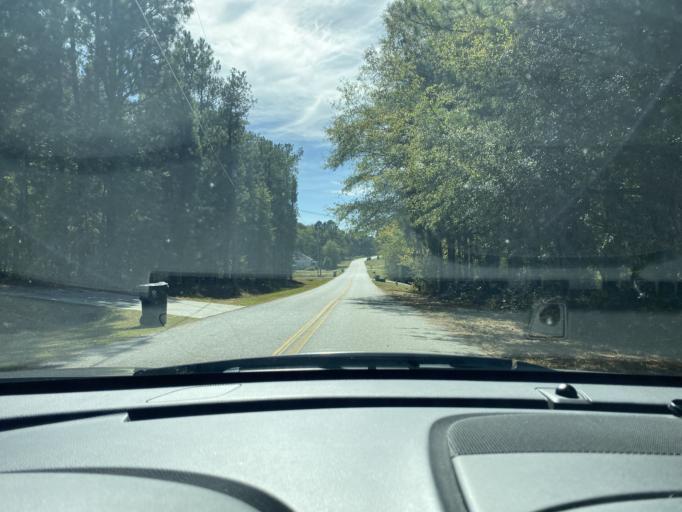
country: US
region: Georgia
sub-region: Walton County
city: Loganville
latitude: 33.8763
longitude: -83.9033
